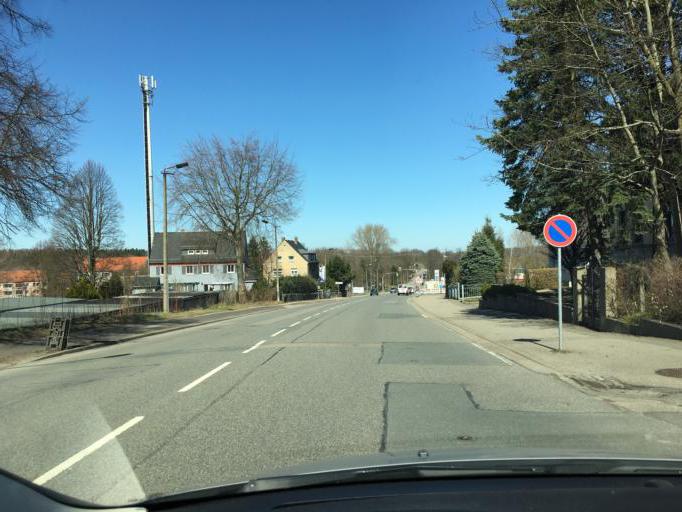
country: DE
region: Saxony
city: Limbach-Oberfrohna
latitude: 50.8622
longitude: 12.7696
